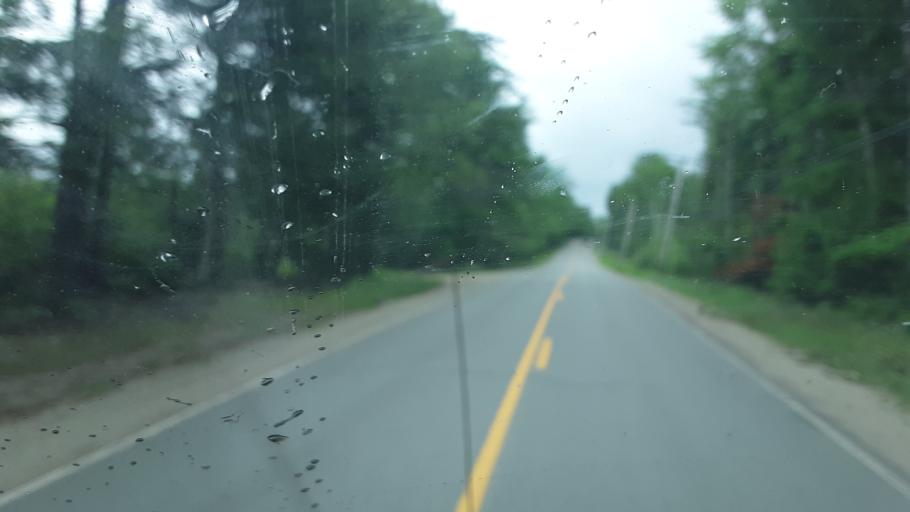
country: US
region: Maine
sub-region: Penobscot County
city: Millinocket
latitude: 45.6839
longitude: -68.7710
